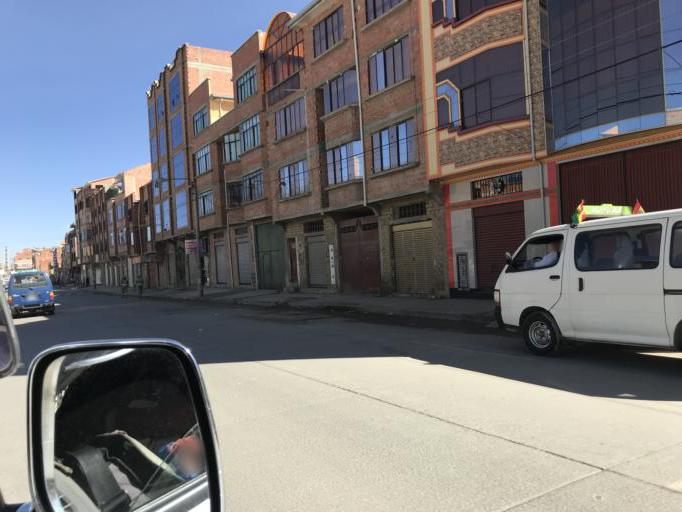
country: BO
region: La Paz
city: La Paz
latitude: -16.4861
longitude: -68.2032
